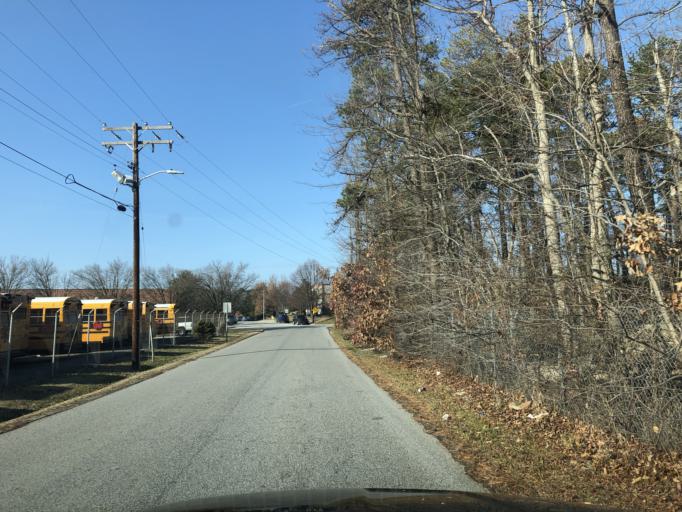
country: US
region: Maryland
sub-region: Anne Arundel County
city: Odenton
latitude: 39.0968
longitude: -76.6980
